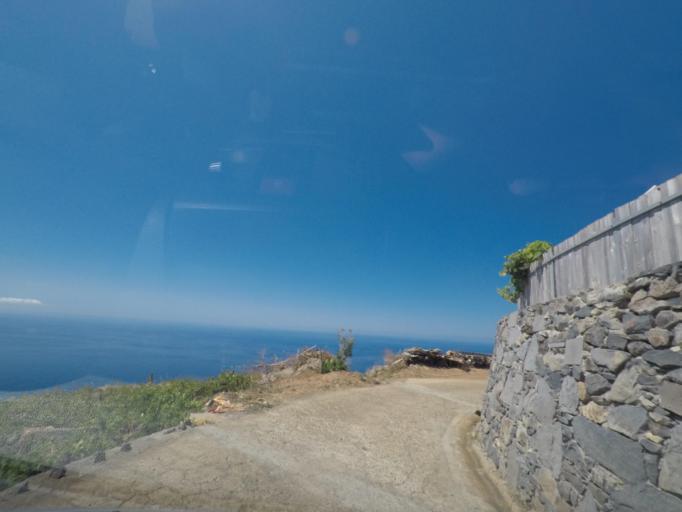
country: PT
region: Madeira
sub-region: Calheta
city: Faja da Ovelha
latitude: 32.7585
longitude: -17.2194
